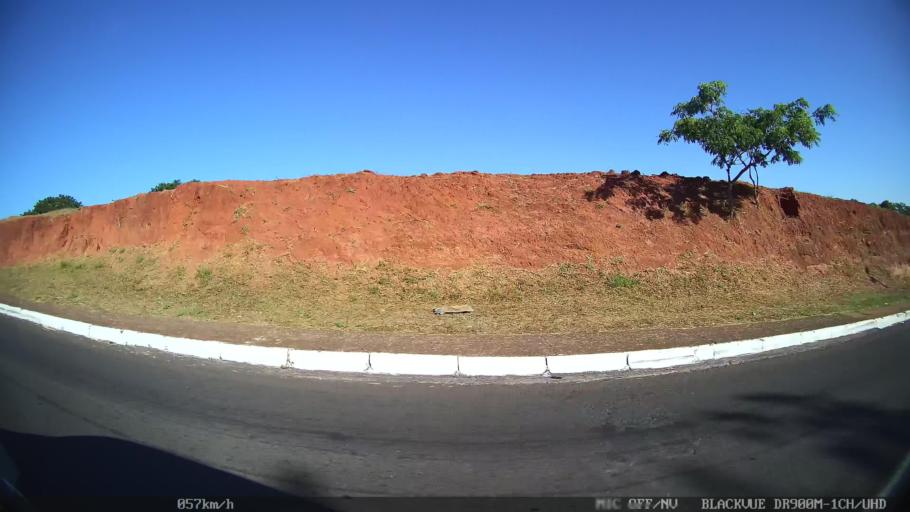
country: BR
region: Sao Paulo
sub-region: Olimpia
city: Olimpia
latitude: -20.7387
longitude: -48.9001
